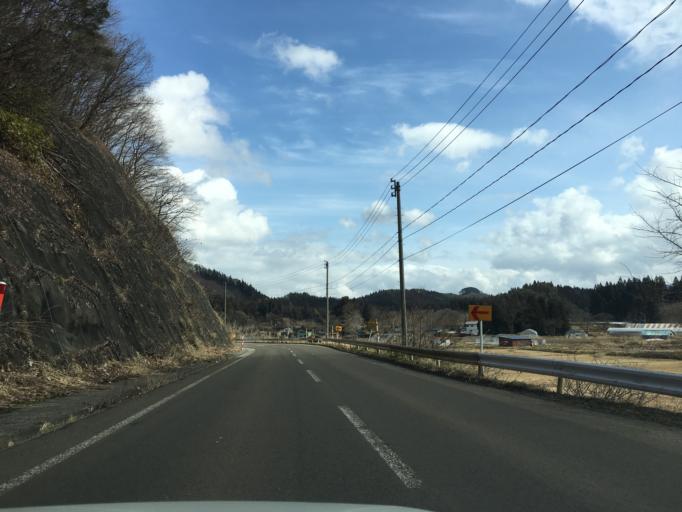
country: JP
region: Akita
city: Odate
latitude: 40.1946
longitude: 140.5317
